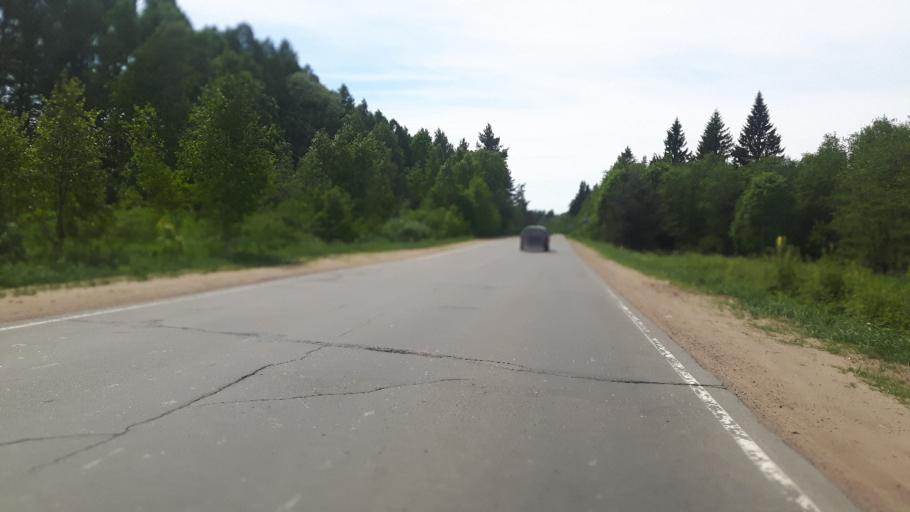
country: RU
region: Leningrad
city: Ust'-Luga
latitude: 59.6399
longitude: 28.2892
